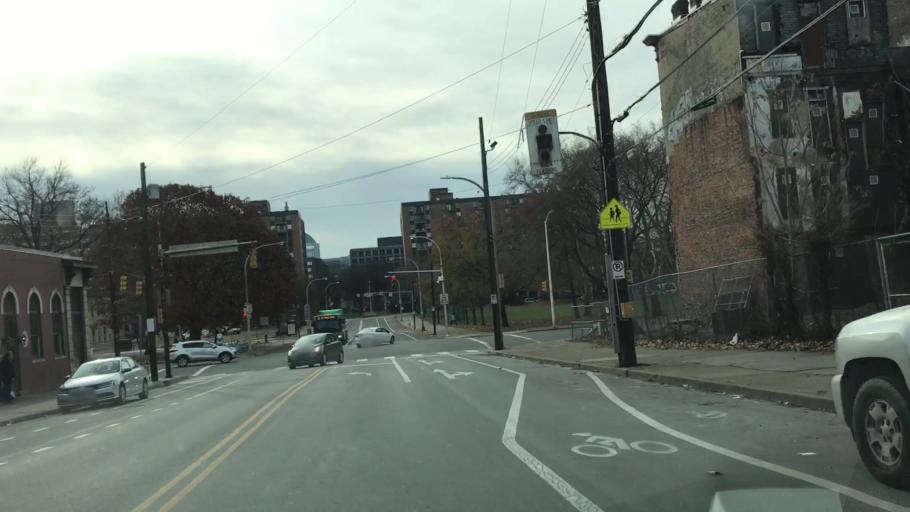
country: US
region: Pennsylvania
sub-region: Allegheny County
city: Pittsburgh
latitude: 40.4559
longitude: -80.0068
